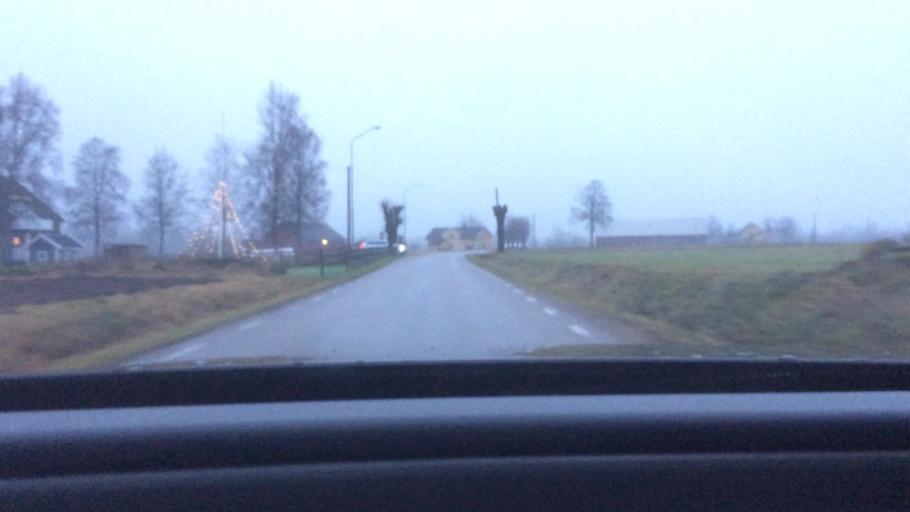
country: SE
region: Vaestra Goetaland
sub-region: Ulricehamns Kommun
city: Ulricehamn
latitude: 57.9496
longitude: 13.3861
